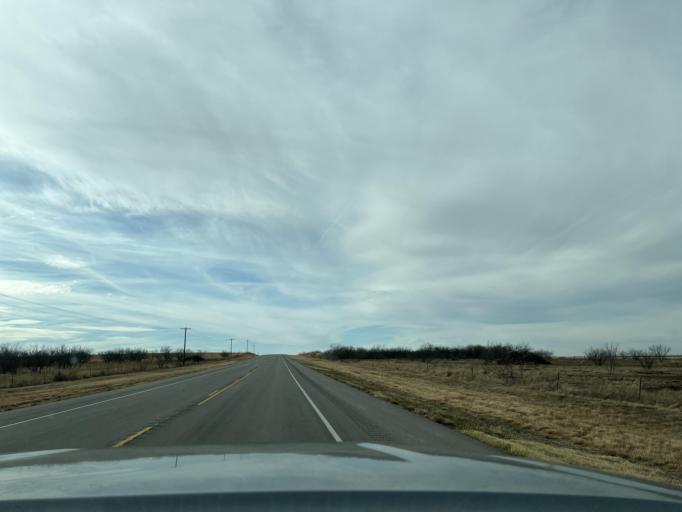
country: US
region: Texas
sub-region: Jones County
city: Anson
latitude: 32.7505
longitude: -99.6756
